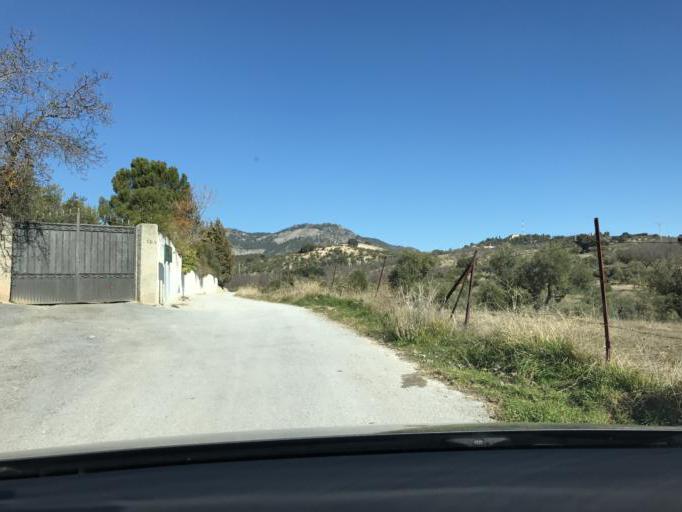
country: ES
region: Andalusia
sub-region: Provincia de Granada
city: Viznar
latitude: 37.2133
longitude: -3.5556
